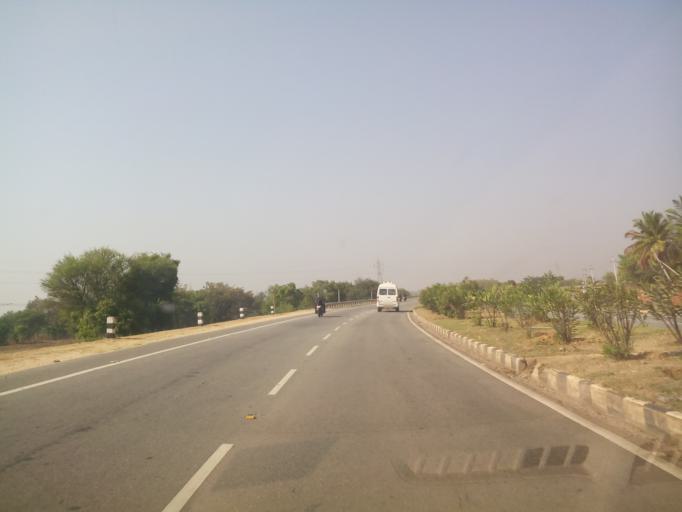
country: IN
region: Karnataka
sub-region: Tumkur
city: Kunigal
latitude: 13.0244
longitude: 77.0744
